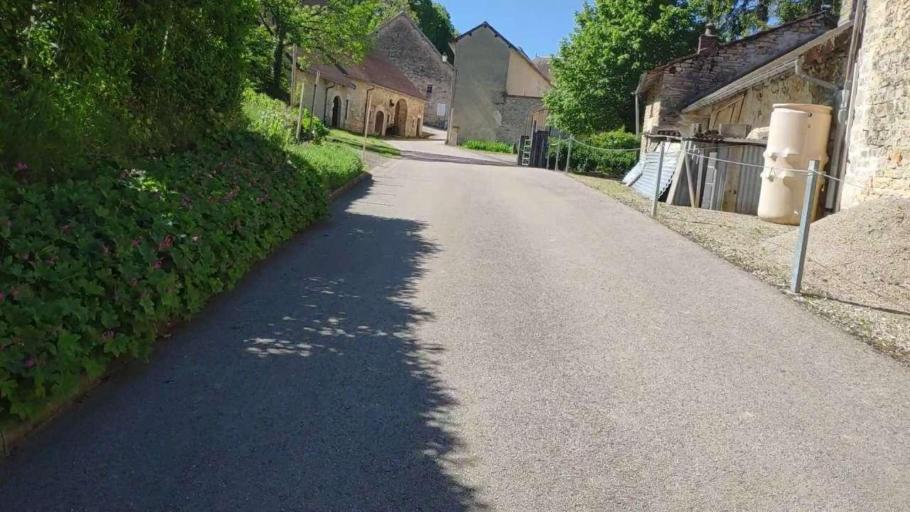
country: FR
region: Franche-Comte
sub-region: Departement du Jura
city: Clairvaux-les-Lacs
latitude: 46.7007
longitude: 5.7324
